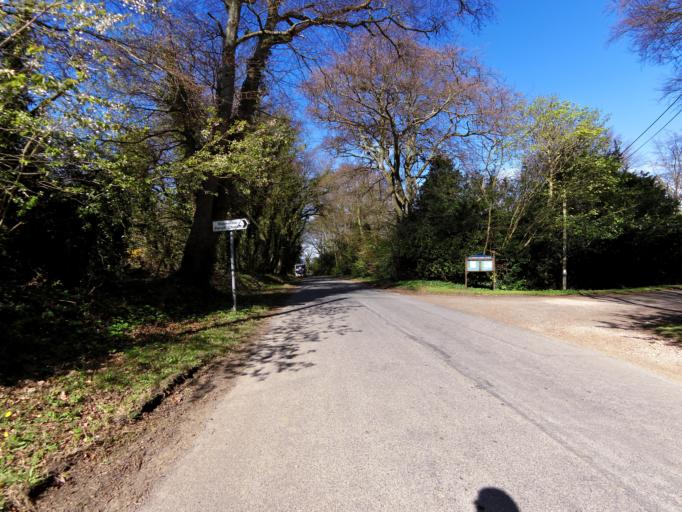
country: GB
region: Scotland
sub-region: Dundee City
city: Dundee
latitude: 56.4084
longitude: -3.0248
